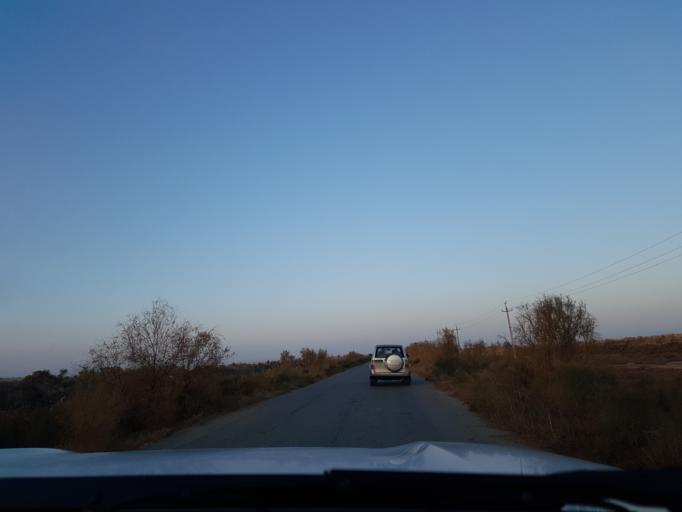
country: TM
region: Dasoguz
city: Koeneuergench
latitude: 41.8441
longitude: 58.6415
